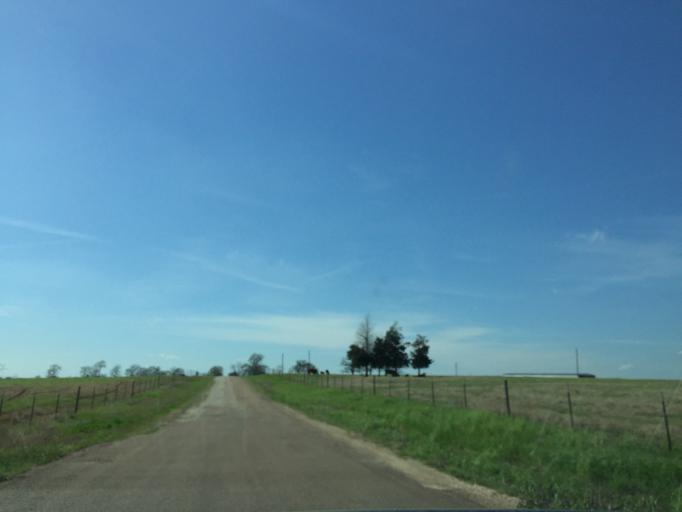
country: US
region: Texas
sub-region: Milam County
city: Thorndale
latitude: 30.5772
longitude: -97.1735
